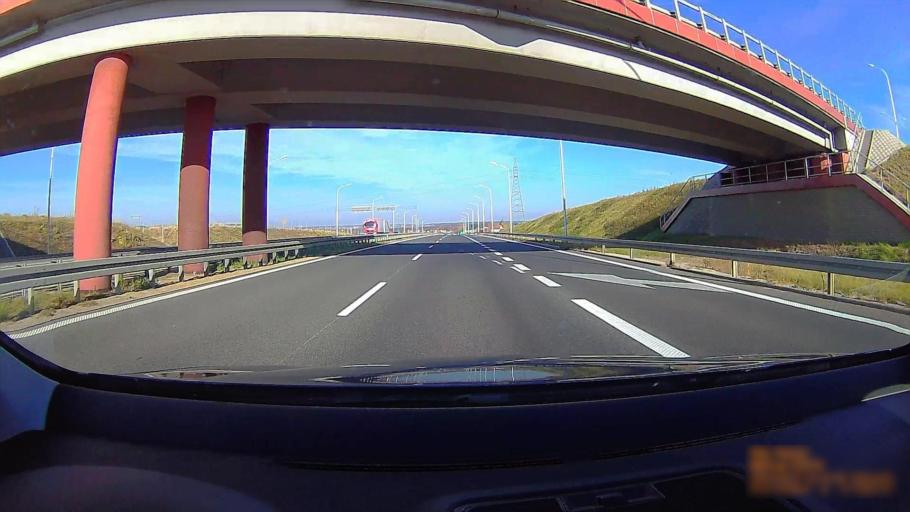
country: PL
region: Greater Poland Voivodeship
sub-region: Powiat ostrowski
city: Przygodzice
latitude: 51.6305
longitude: 17.8692
